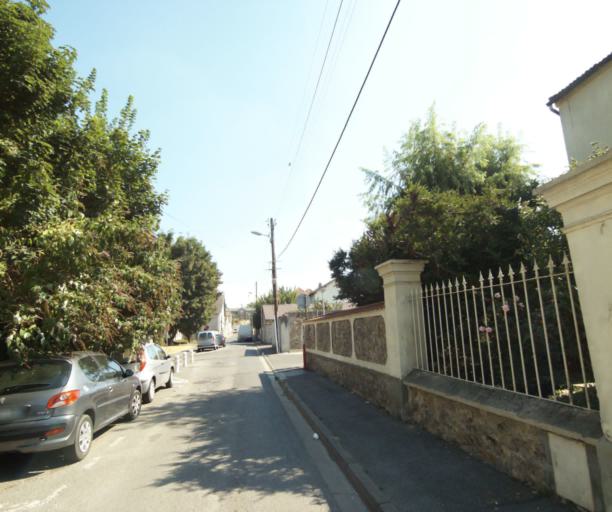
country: FR
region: Ile-de-France
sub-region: Departement de Seine-et-Marne
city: Pomponne
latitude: 48.8774
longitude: 2.6962
